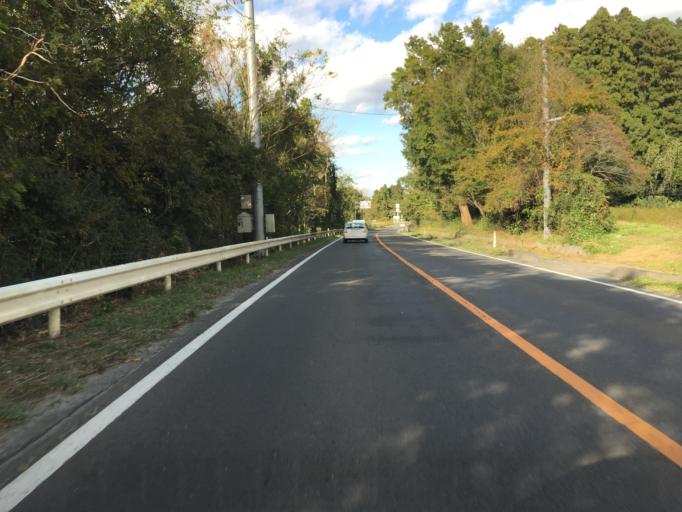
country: JP
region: Miyagi
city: Marumori
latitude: 37.9070
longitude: 140.9012
